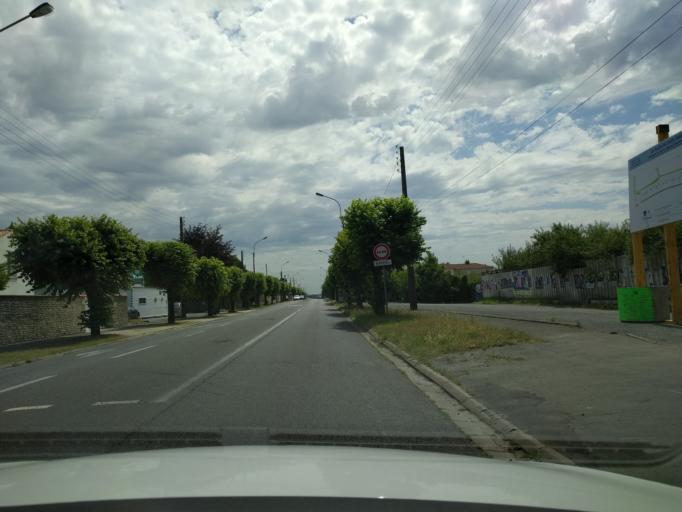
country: FR
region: Poitou-Charentes
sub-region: Departement des Deux-Sevres
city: Niort
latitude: 46.3385
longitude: -0.4824
